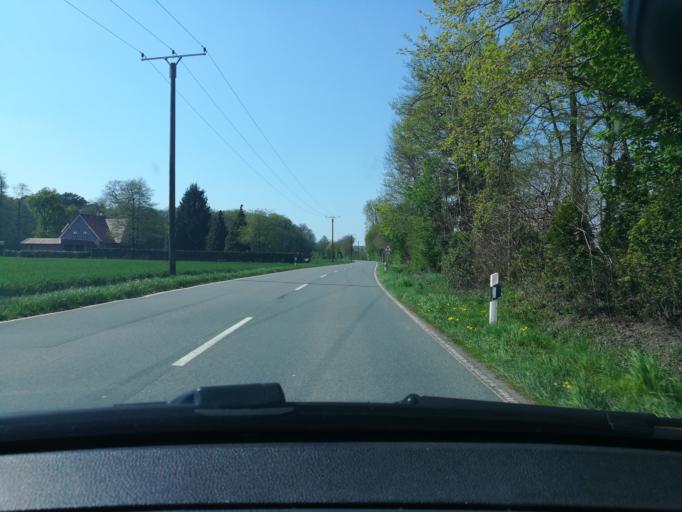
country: DE
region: North Rhine-Westphalia
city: Versmold
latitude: 52.0096
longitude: 8.1603
